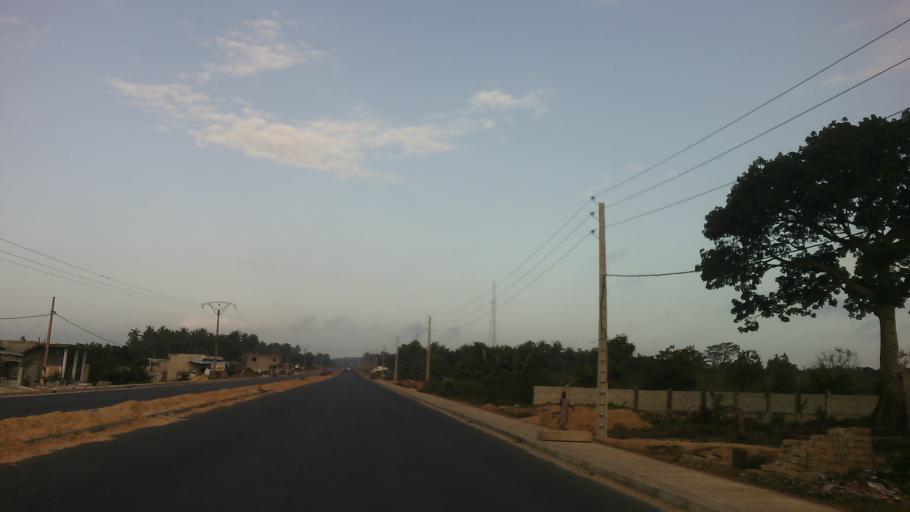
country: BJ
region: Atlantique
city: Hevie
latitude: 6.3831
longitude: 2.1836
